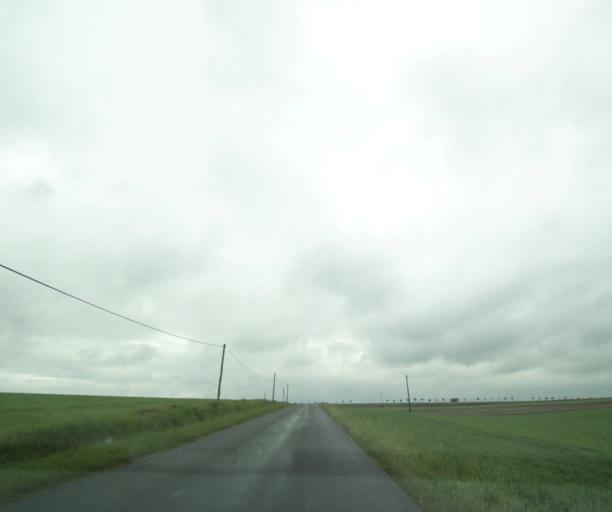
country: FR
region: Poitou-Charentes
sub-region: Departement de la Charente-Maritime
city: Perignac
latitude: 45.6482
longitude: -0.5227
